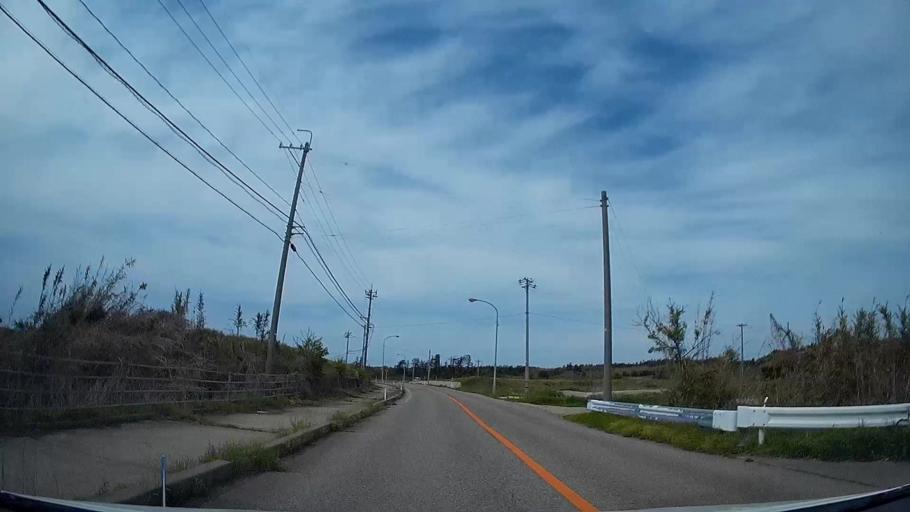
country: JP
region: Ishikawa
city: Hakui
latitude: 37.0332
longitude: 136.7470
